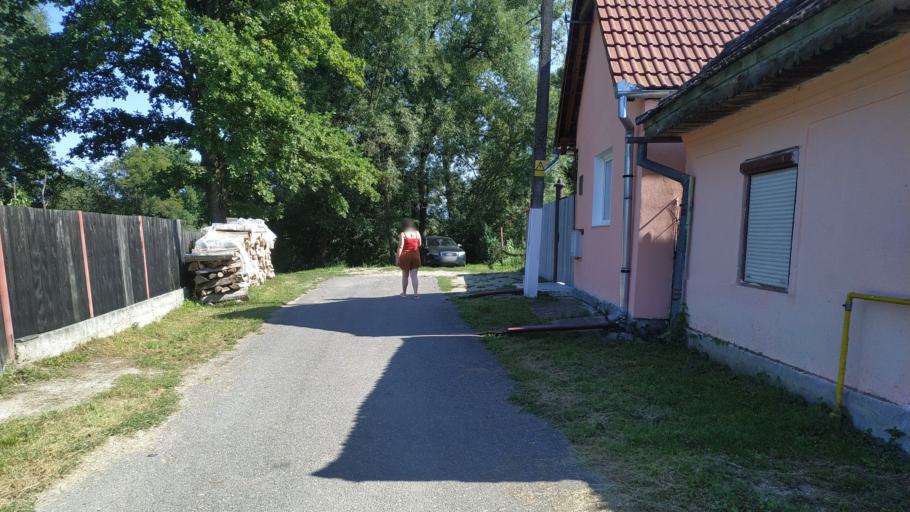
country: RO
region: Brasov
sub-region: Comuna Beclean
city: Beclean
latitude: 45.8288
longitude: 24.9224
